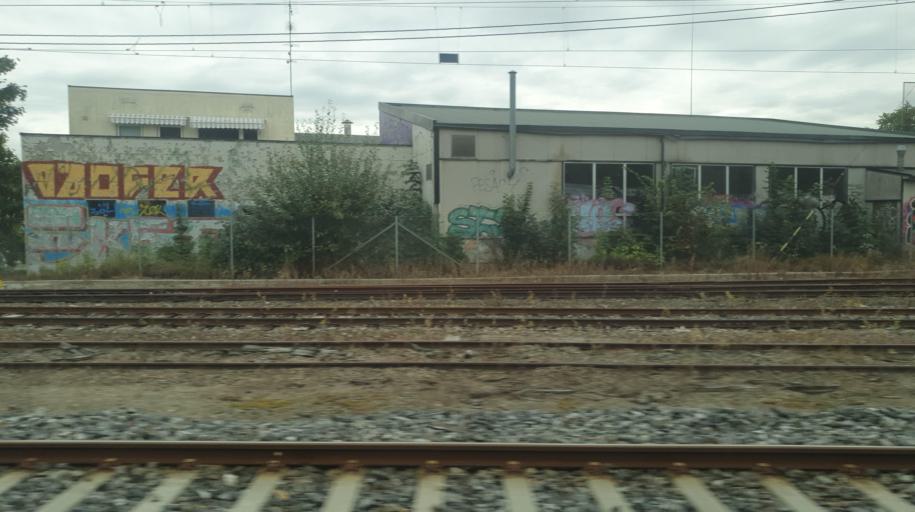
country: NO
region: Vestfold
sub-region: Tonsberg
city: Tonsberg
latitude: 59.2745
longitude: 10.4075
